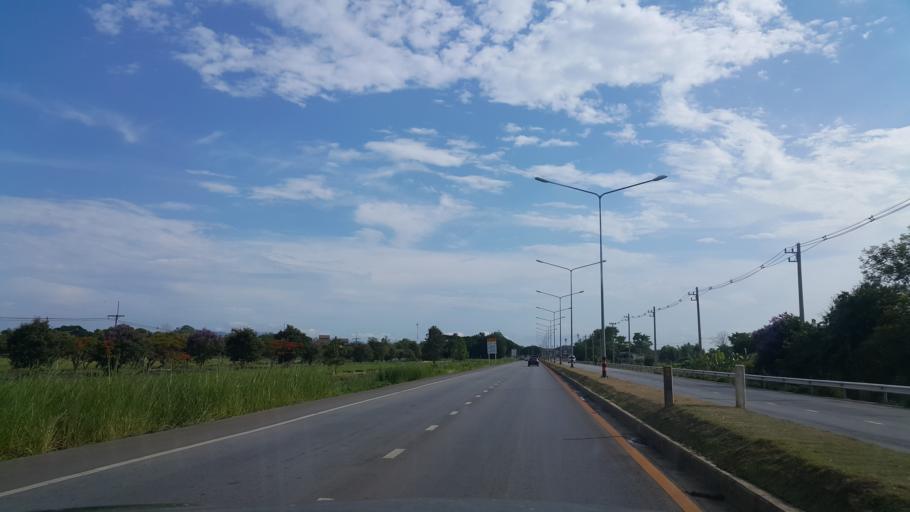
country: TH
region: Chiang Rai
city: Chiang Rai
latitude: 19.9375
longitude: 99.8668
